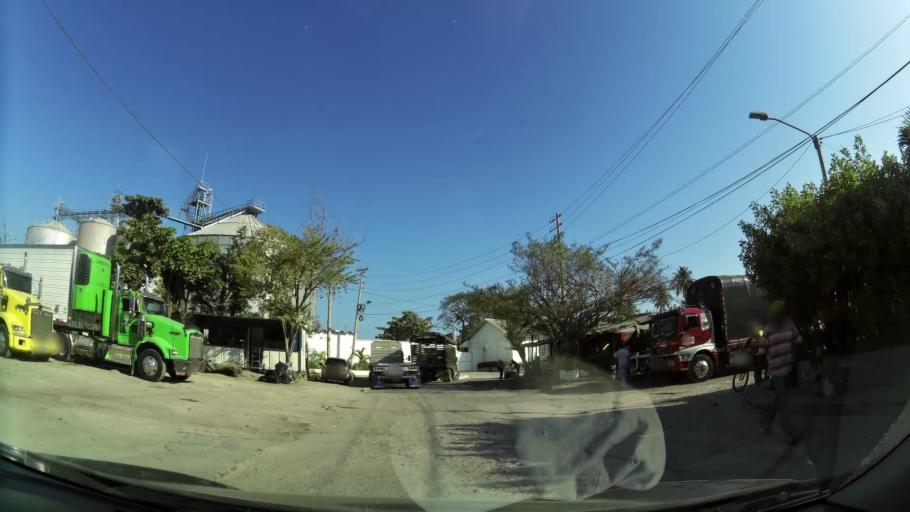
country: CO
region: Bolivar
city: Cartagena
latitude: 10.3997
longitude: -75.5228
